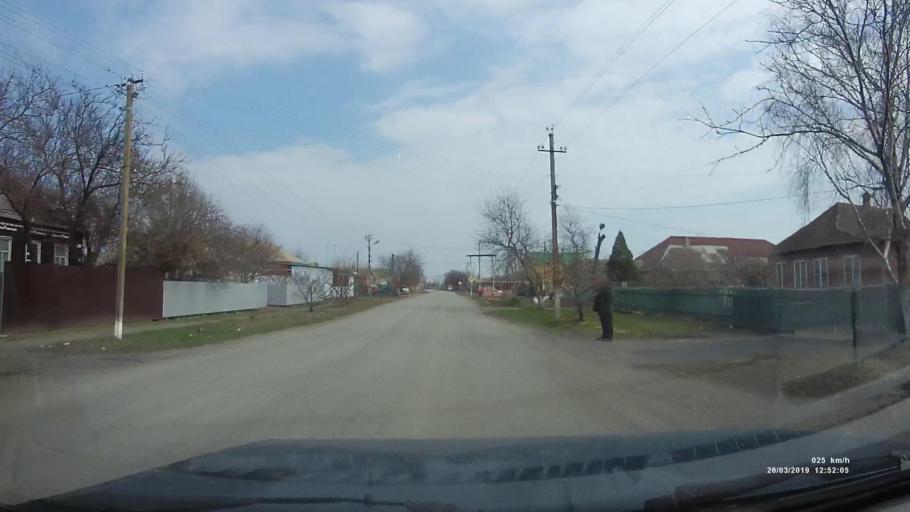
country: RU
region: Rostov
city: Novobessergenovka
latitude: 47.1589
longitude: 38.7102
